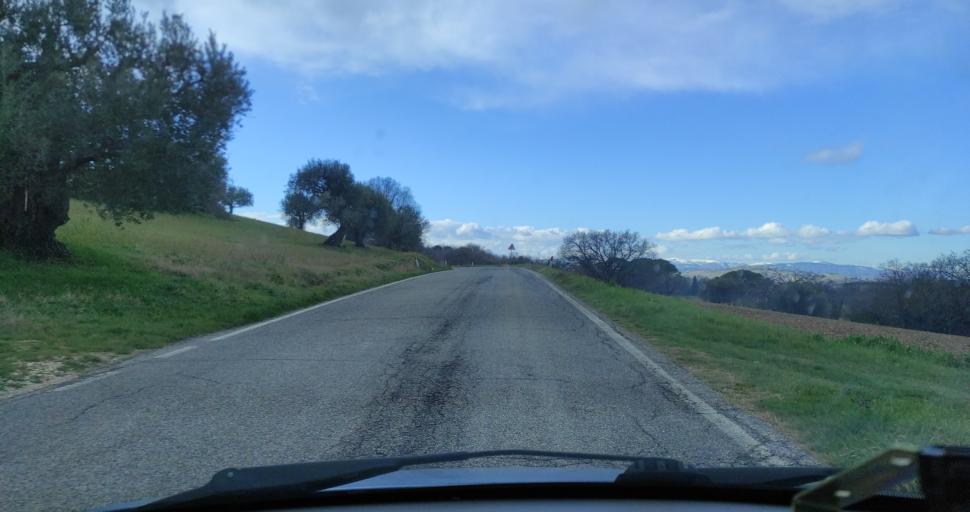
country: IT
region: The Marches
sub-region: Provincia di Macerata
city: Casette Verdini
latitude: 43.2131
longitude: 13.4190
